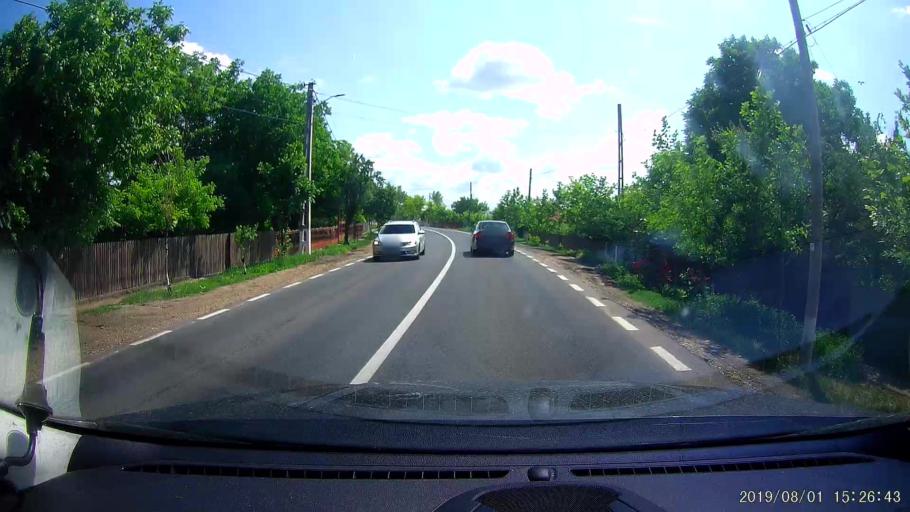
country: RO
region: Braila
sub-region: Comuna Viziru
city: Viziru
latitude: 45.0073
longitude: 27.7184
